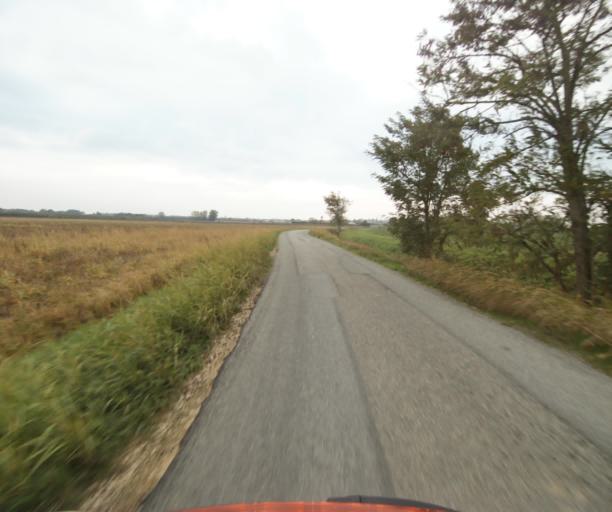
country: FR
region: Midi-Pyrenees
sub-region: Departement du Tarn-et-Garonne
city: Verdun-sur-Garonne
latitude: 43.8156
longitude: 1.2223
